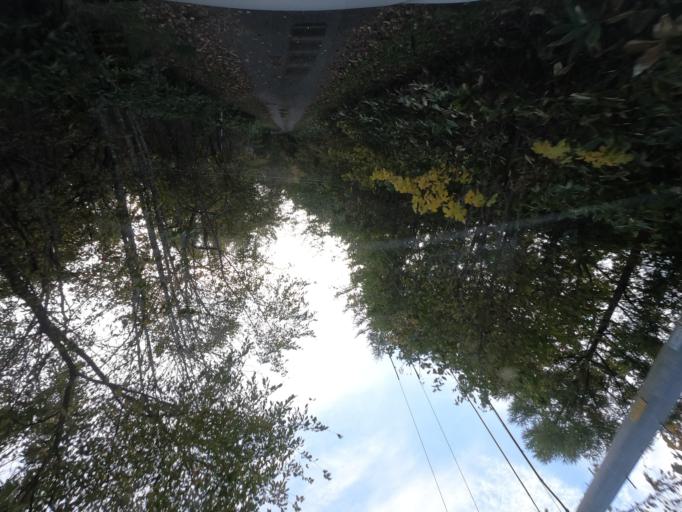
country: JP
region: Hokkaido
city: Obihiro
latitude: 42.5867
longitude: 143.3146
